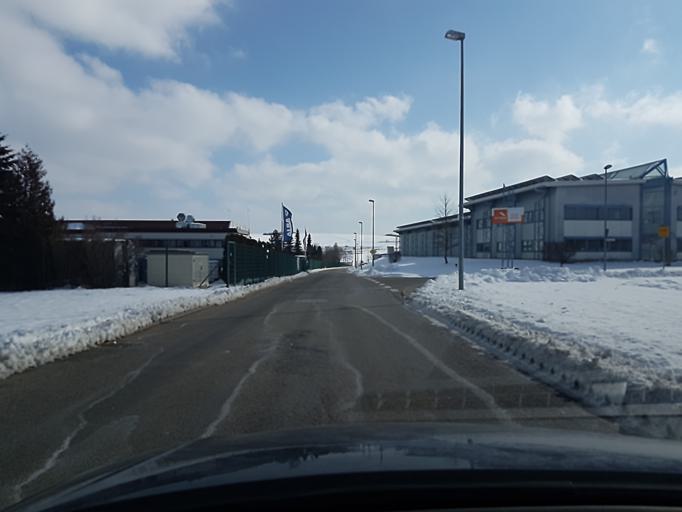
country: DE
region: Baden-Wuerttemberg
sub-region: Freiburg Region
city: Dunningen
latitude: 48.2212
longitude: 8.5034
